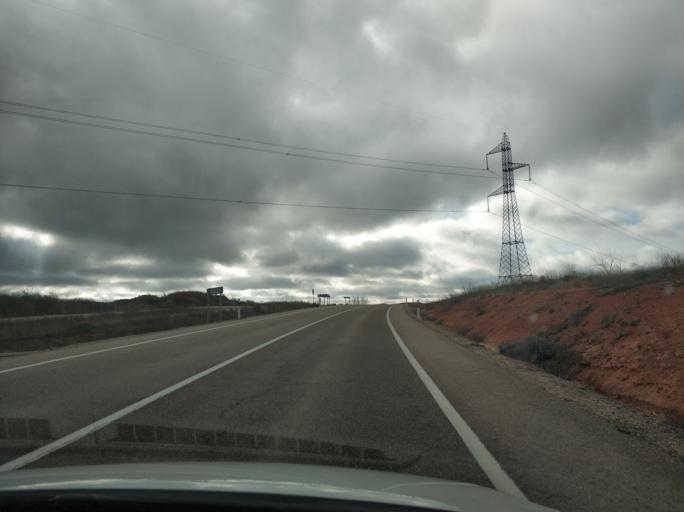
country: ES
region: Castille and Leon
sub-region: Provincia de Soria
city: San Esteban de Gormaz
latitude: 41.5649
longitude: -3.2444
